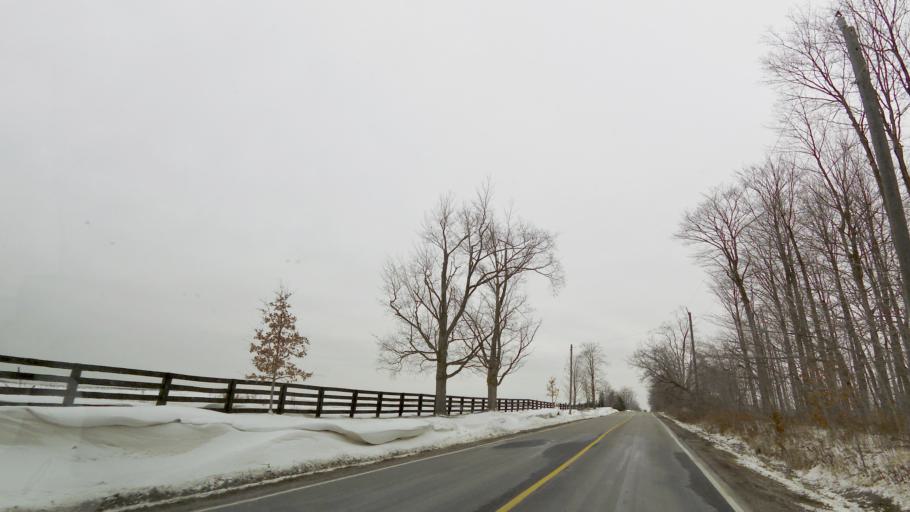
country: CA
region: Ontario
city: Vaughan
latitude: 43.8833
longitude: -79.5964
